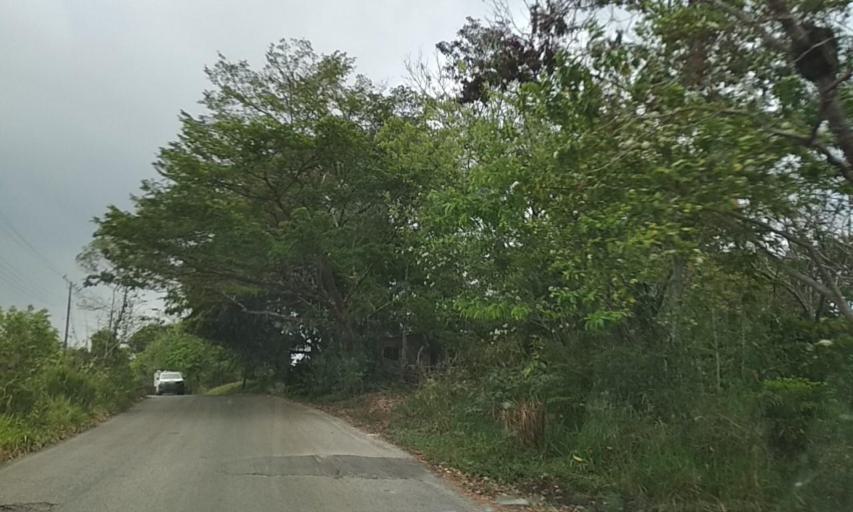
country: MX
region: Veracruz
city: Las Choapas
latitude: 17.7506
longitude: -94.1112
